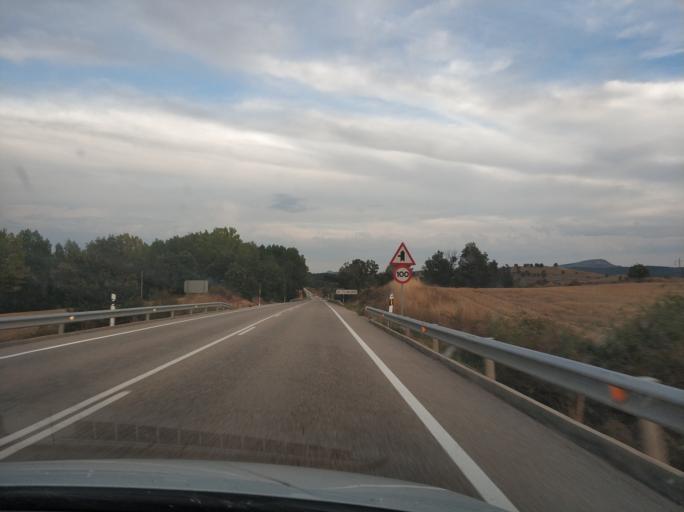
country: ES
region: Castille and Leon
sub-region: Provincia de Burgos
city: Pinilla de los Barruecos
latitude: 41.8977
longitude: -3.2670
